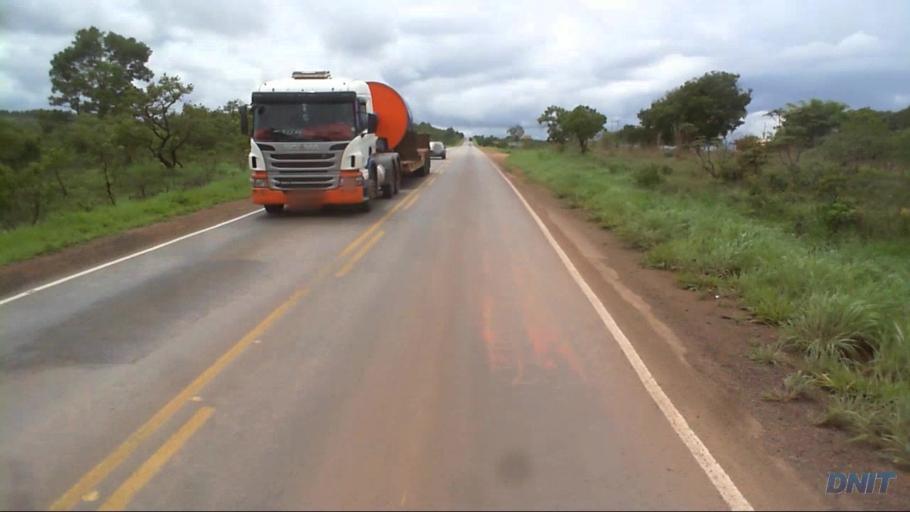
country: BR
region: Goias
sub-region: Padre Bernardo
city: Padre Bernardo
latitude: -15.3733
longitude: -48.2176
